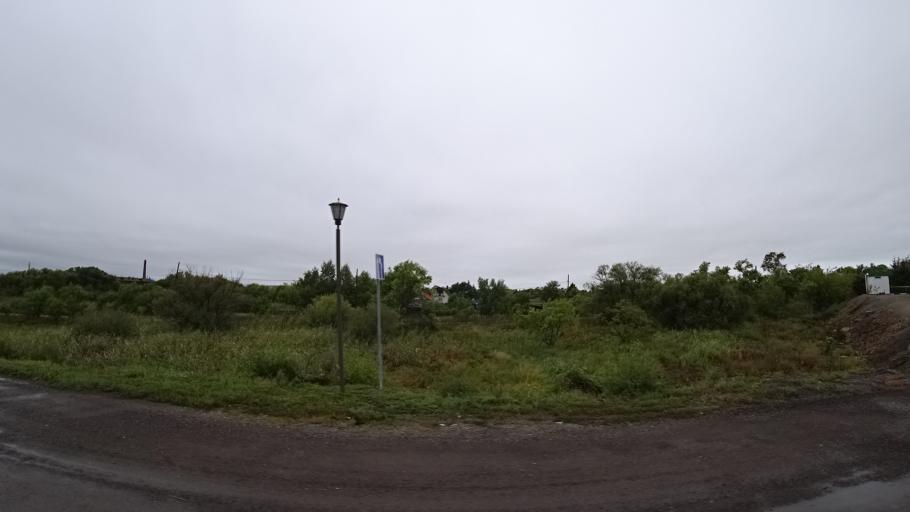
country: RU
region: Primorskiy
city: Monastyrishche
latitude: 44.2142
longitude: 132.4498
